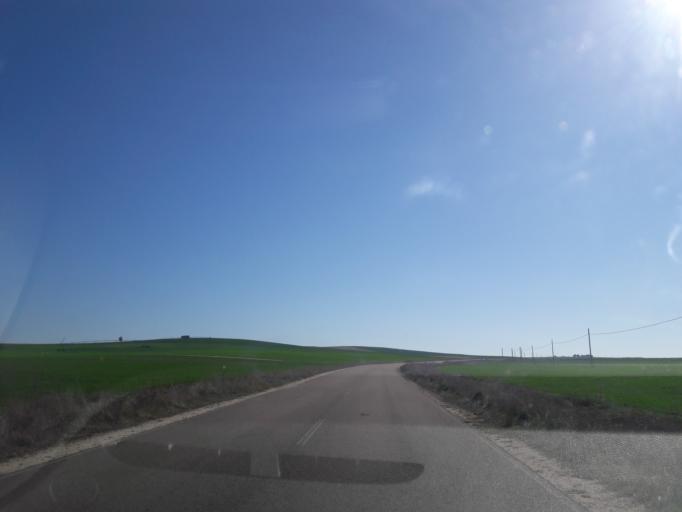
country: ES
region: Castille and Leon
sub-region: Provincia de Salamanca
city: Tordillos
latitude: 40.8512
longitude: -5.3303
